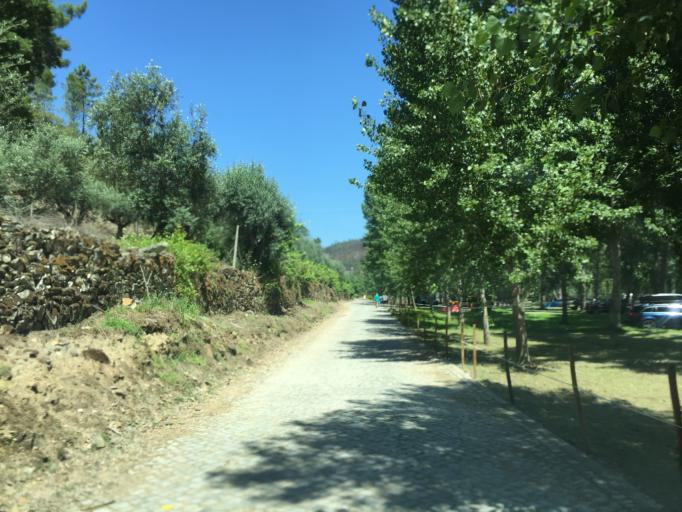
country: PT
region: Coimbra
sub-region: Pampilhosa da Serra
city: Pampilhosa da Serra
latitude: 40.0114
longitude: -7.8458
